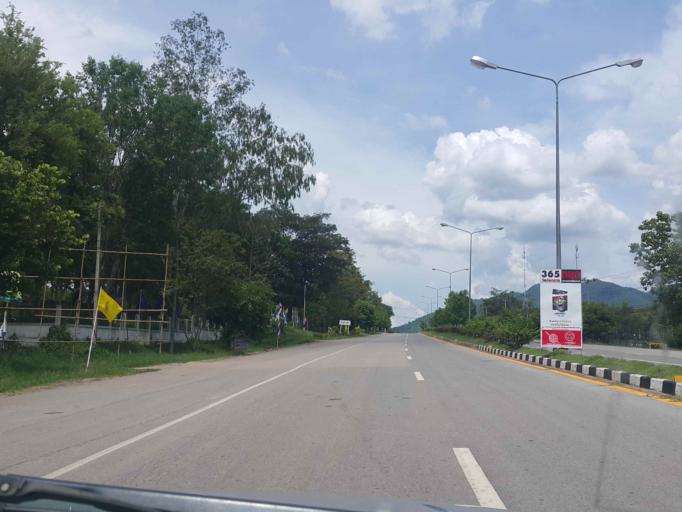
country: TH
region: Nan
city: Ban Luang
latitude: 18.8501
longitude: 100.4367
